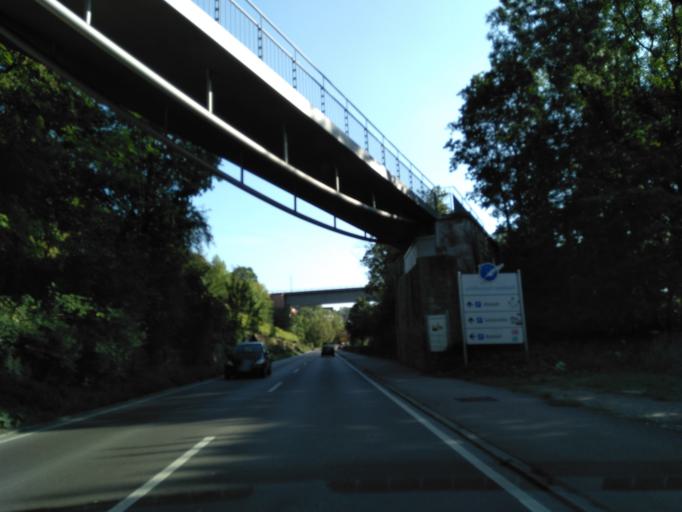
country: DE
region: Baden-Wuerttemberg
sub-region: Regierungsbezirk Stuttgart
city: Marbach am Neckar
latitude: 48.9446
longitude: 9.2529
